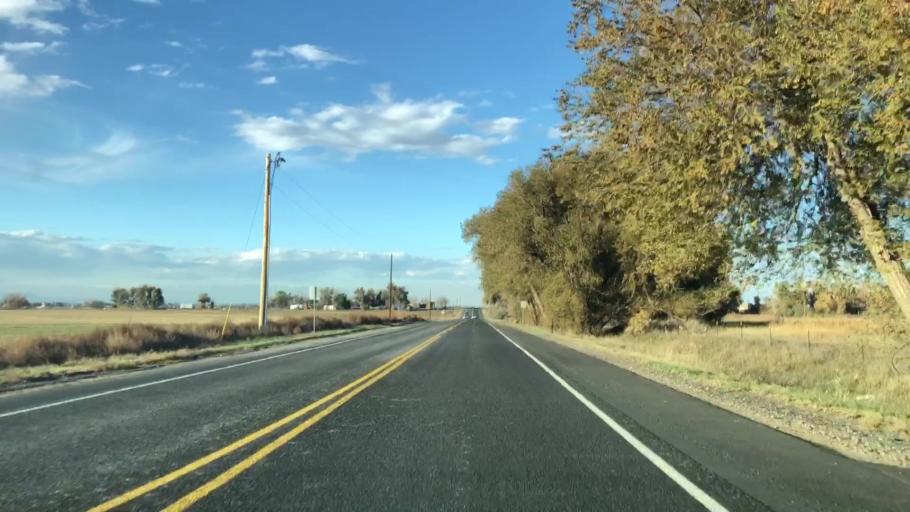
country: US
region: Colorado
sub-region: Larimer County
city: Loveland
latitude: 40.4672
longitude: -105.0203
